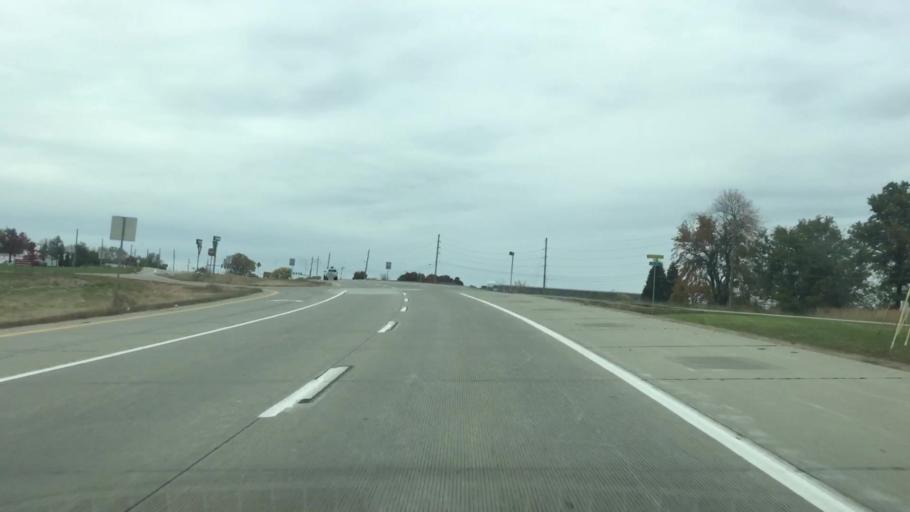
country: US
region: Missouri
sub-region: Jackson County
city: Lees Summit
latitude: 38.8920
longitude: -94.3732
